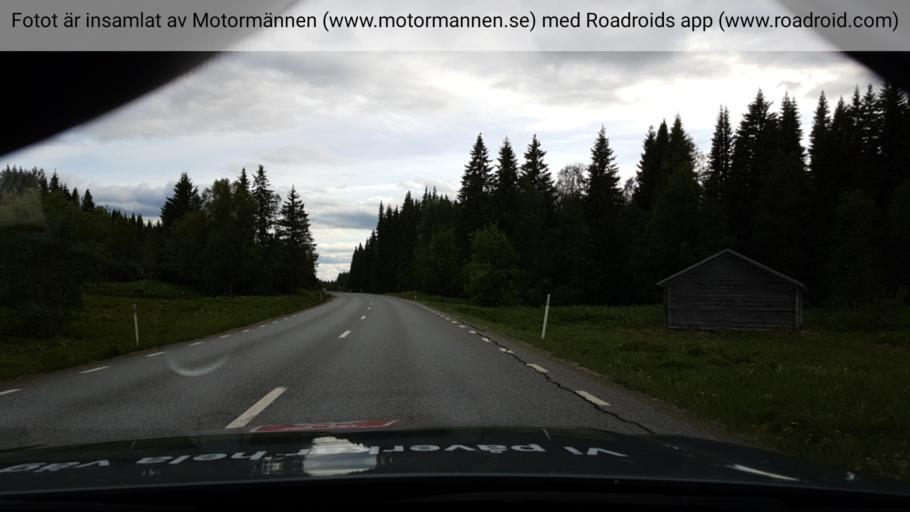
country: SE
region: Jaemtland
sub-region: OEstersunds Kommun
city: Lit
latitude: 63.4916
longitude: 15.2459
